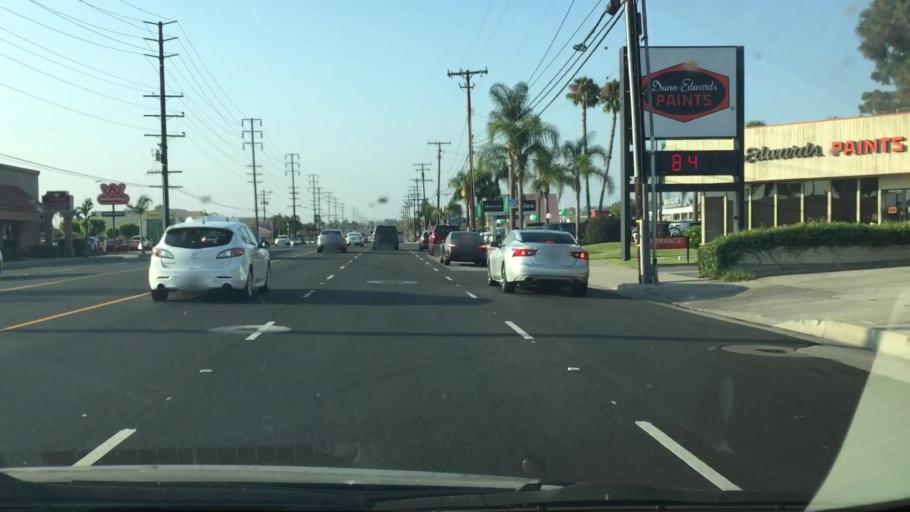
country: US
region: California
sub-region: Orange County
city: Villa Park
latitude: 33.8192
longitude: -117.8359
